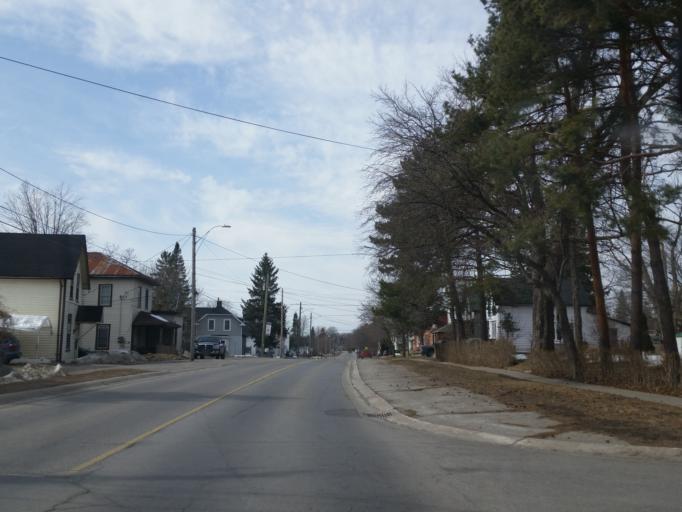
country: CA
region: Ontario
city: Deseronto
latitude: 44.1970
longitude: -77.0516
